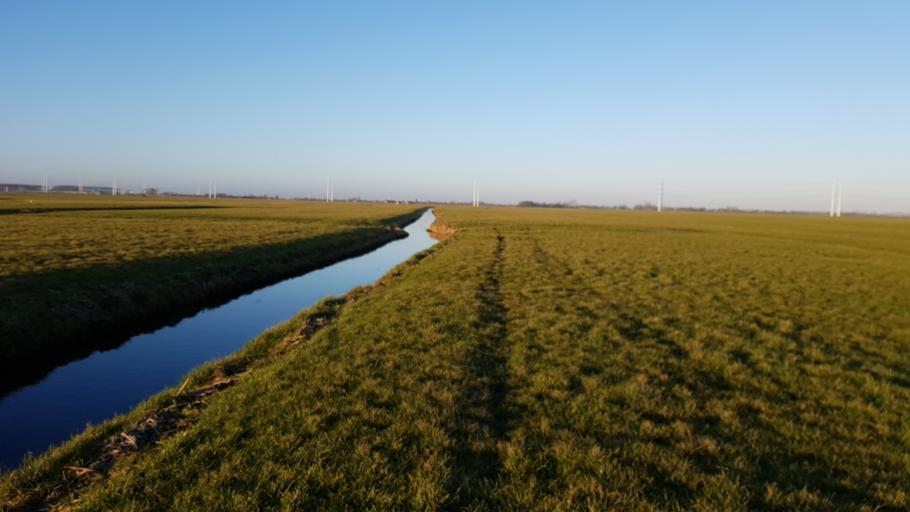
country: NL
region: South Holland
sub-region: Gemeente Leiderdorp
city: Leiderdorp
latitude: 52.1381
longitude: 4.5615
